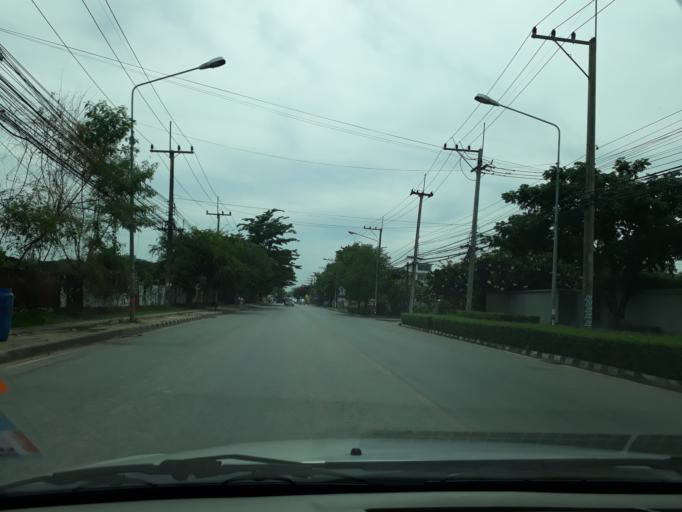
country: TH
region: Khon Kaen
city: Khon Kaen
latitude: 16.4369
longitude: 102.8460
